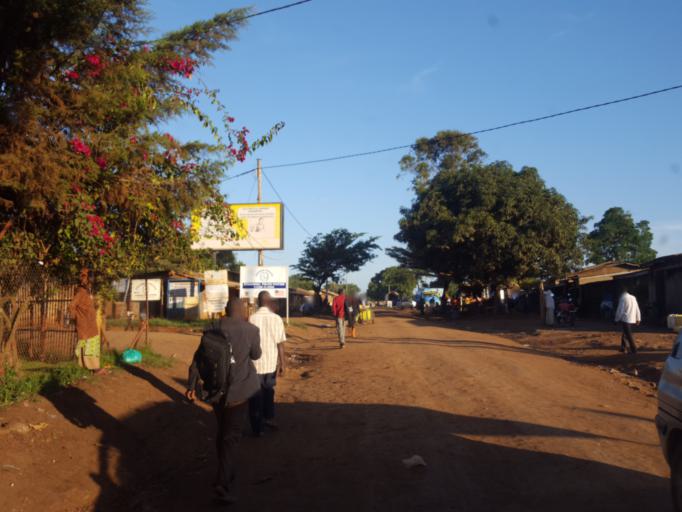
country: UG
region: Western Region
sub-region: Kibale District
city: Kagadi
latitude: 1.1892
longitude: 30.7824
